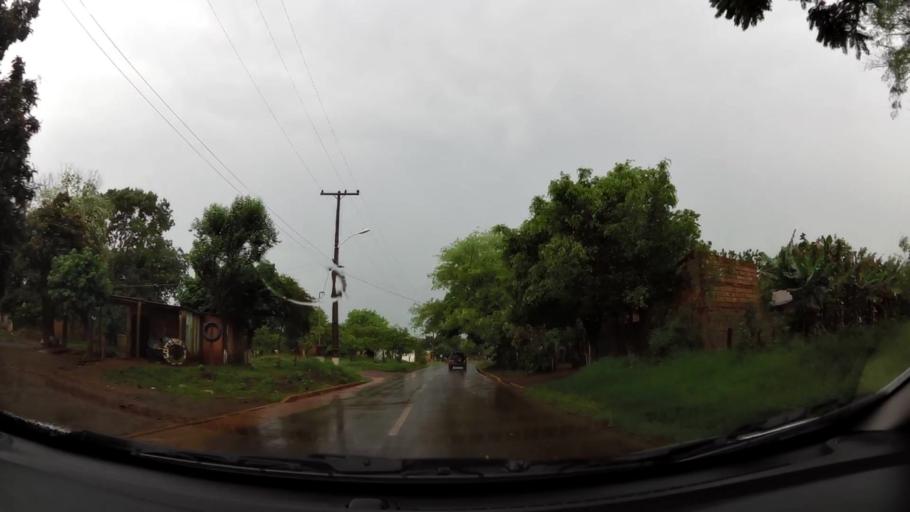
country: PY
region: Alto Parana
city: Presidente Franco
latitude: -25.5510
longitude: -54.6626
